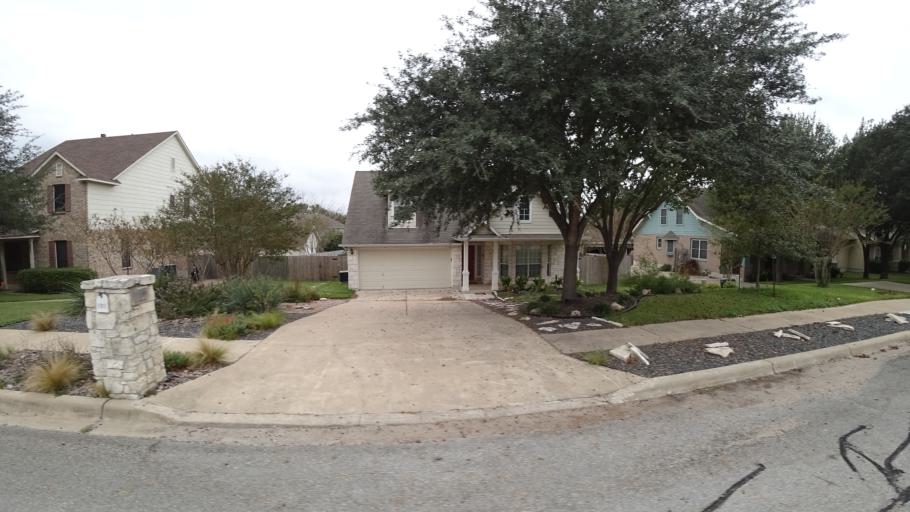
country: US
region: Texas
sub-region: Travis County
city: Pflugerville
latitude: 30.4363
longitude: -97.6242
